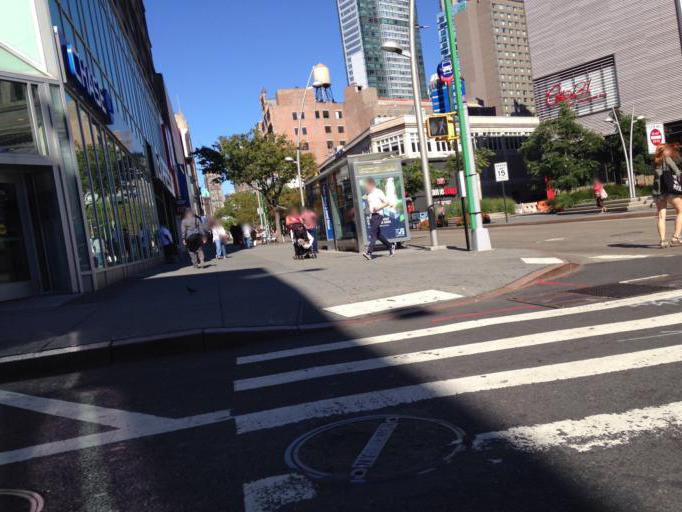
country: US
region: New York
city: New York City
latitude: 40.6897
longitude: -73.9831
